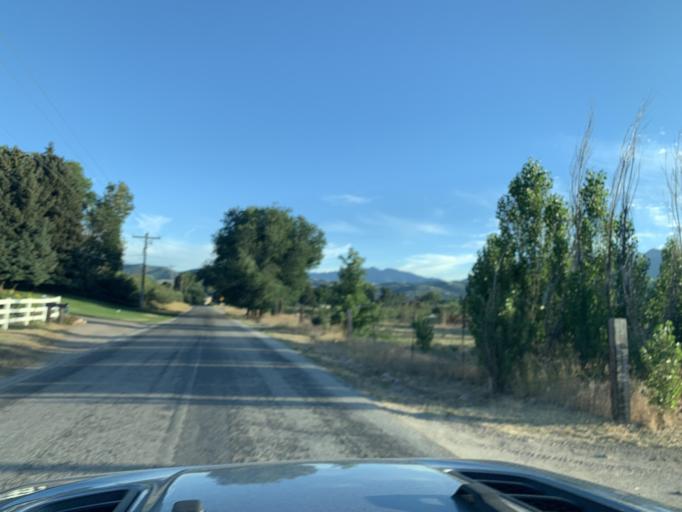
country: US
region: Utah
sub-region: Weber County
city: Wolf Creek
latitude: 41.2851
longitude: -111.7585
